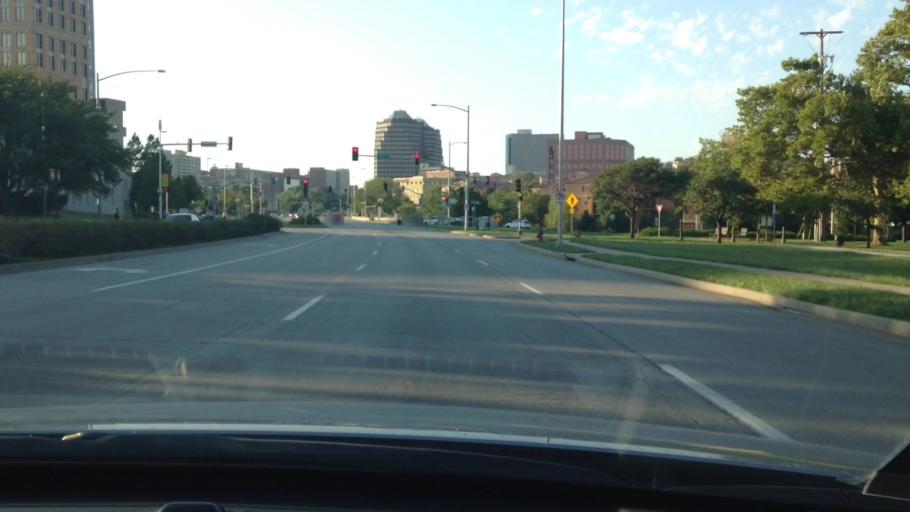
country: US
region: Kansas
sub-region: Johnson County
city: Westwood
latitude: 39.0377
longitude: -94.5845
